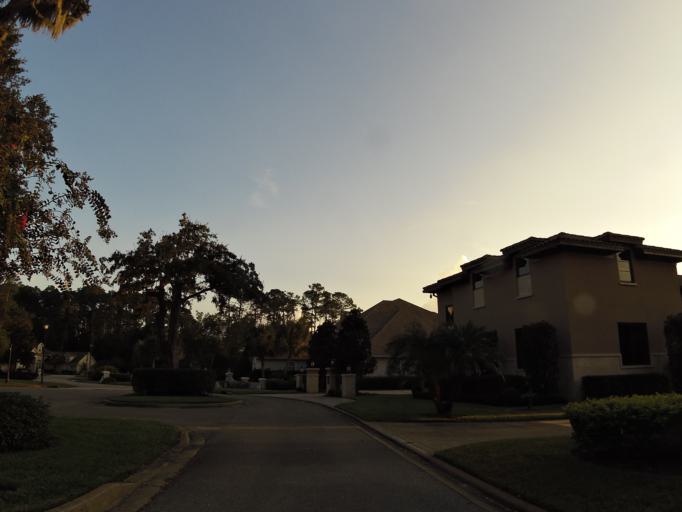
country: US
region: Florida
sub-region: Clay County
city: Orange Park
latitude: 30.1796
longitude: -81.6426
